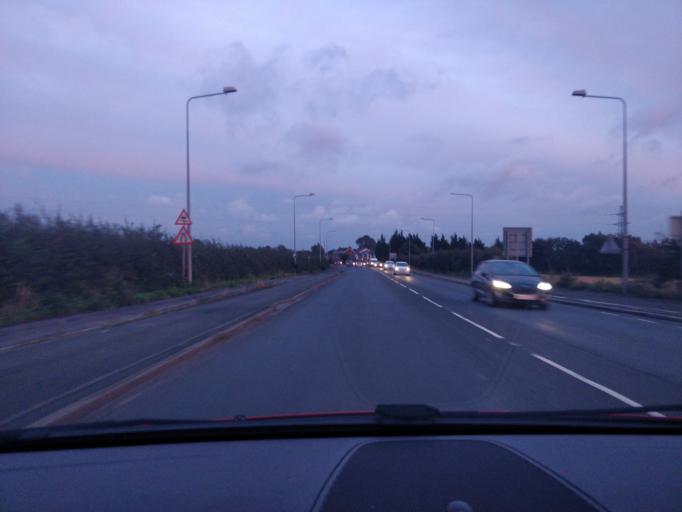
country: GB
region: England
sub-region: Sefton
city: Southport
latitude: 53.6222
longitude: -2.9579
